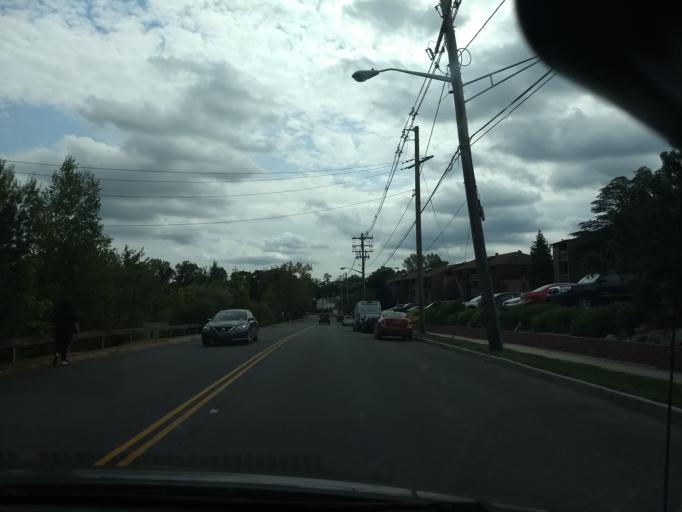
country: US
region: New York
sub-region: Rockland County
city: Monsey
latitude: 41.1051
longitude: -74.0575
